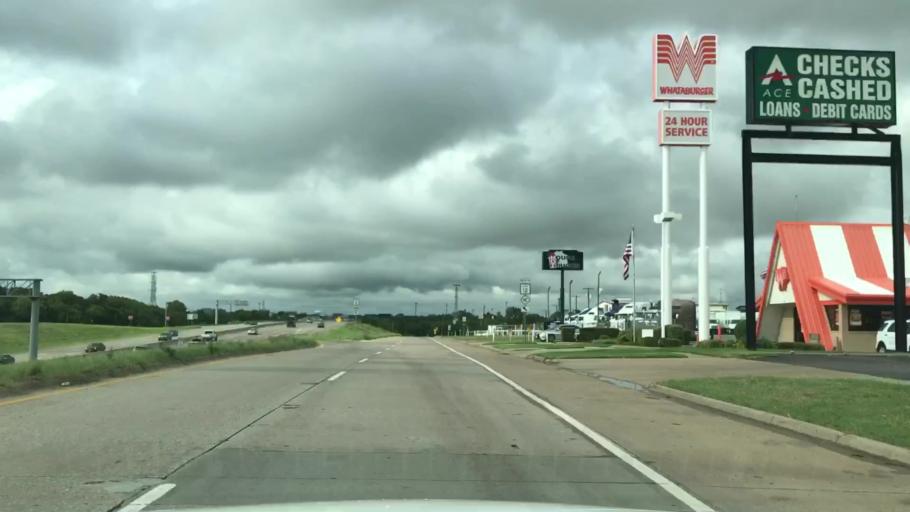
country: US
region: Texas
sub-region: Dallas County
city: Irving
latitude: 32.8580
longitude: -96.9604
